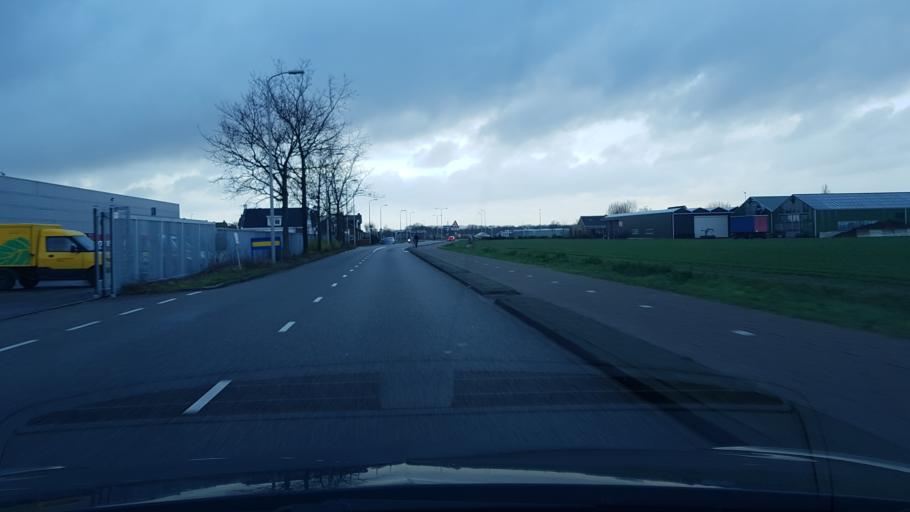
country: NL
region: South Holland
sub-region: Gemeente Lisse
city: Lisse
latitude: 52.2433
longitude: 4.5436
